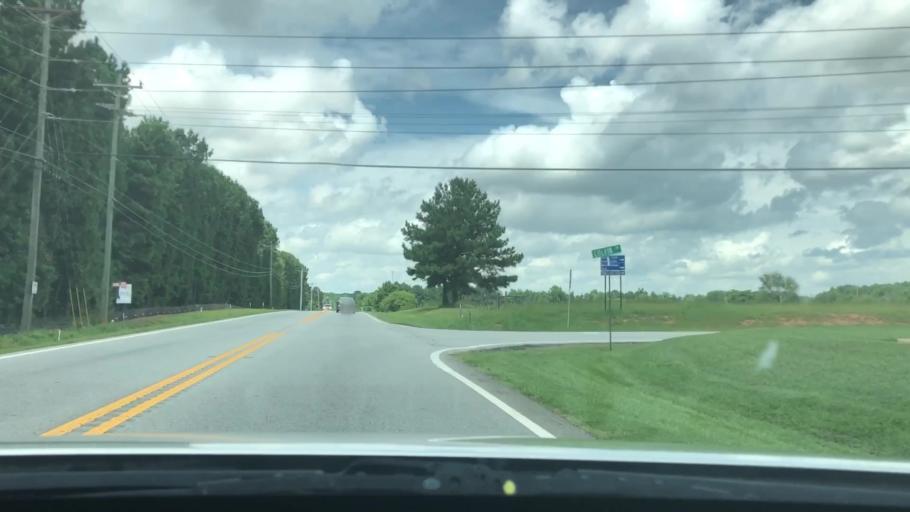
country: US
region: Georgia
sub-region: Henry County
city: Locust Grove
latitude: 33.3682
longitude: -84.1231
